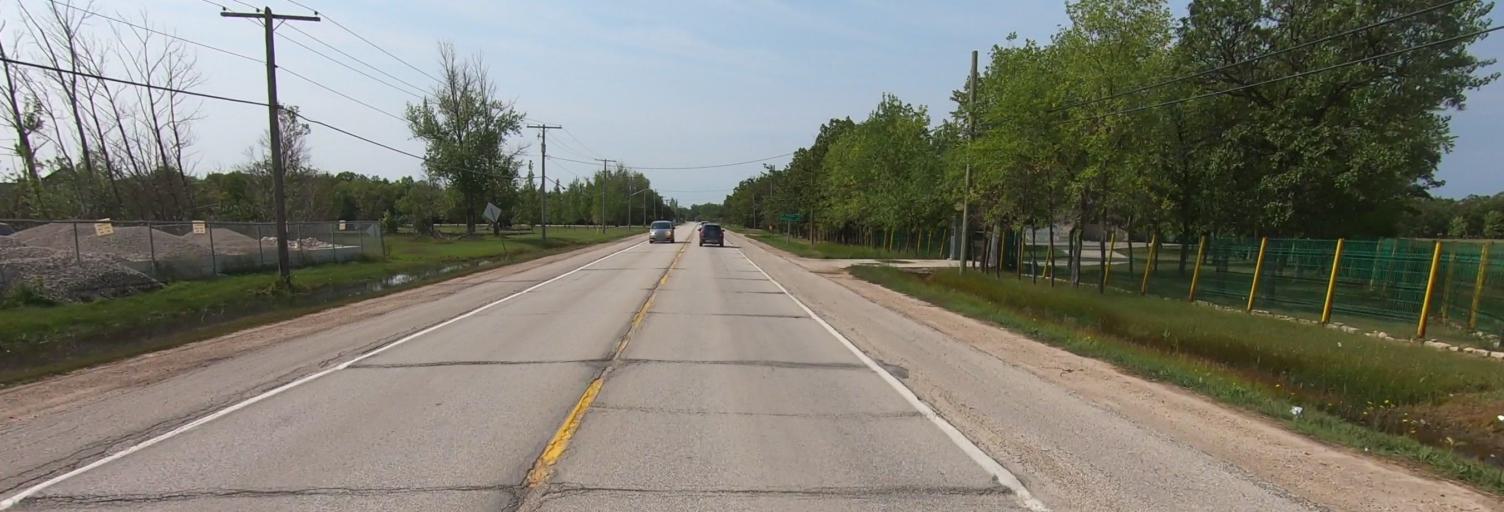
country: CA
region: Manitoba
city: Winnipeg
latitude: 49.7870
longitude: -97.1196
